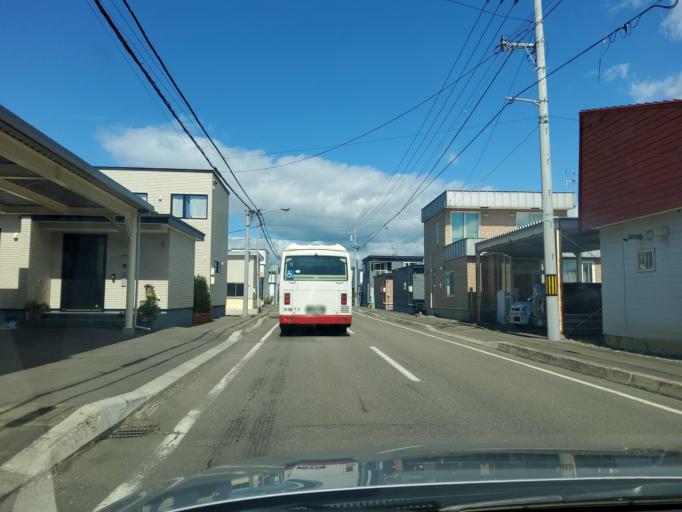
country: JP
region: Hokkaido
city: Obihiro
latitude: 42.9528
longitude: 143.2025
